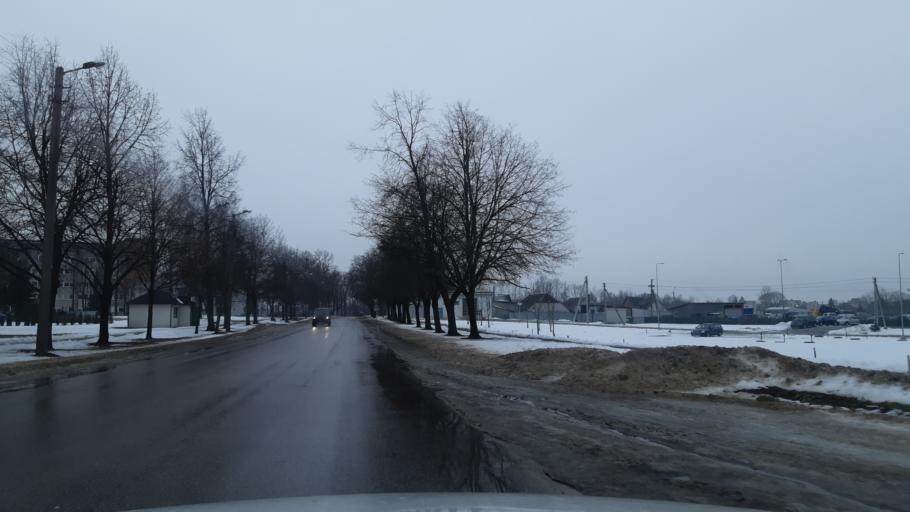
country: LT
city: Vilkaviskis
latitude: 54.6526
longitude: 23.0261
